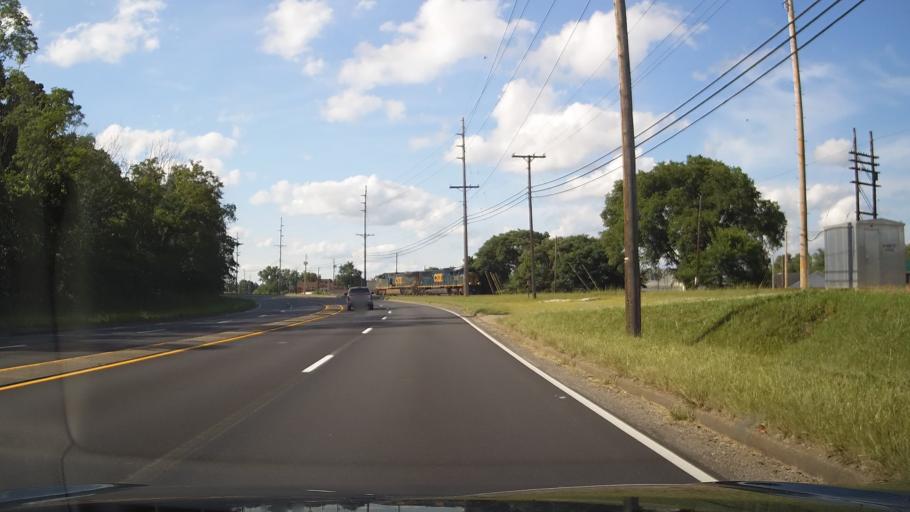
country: US
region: Kentucky
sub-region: Boyd County
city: Catlettsburg
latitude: 38.4127
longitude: -82.5991
